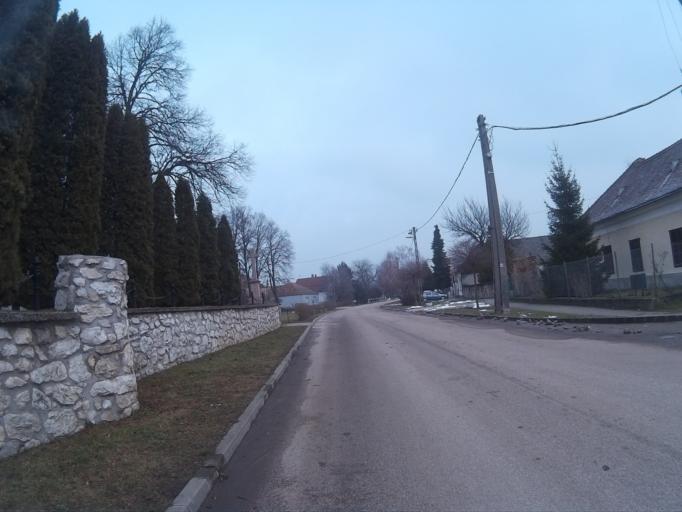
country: HU
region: Komarom-Esztergom
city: Tarjan
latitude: 47.6466
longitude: 18.5110
